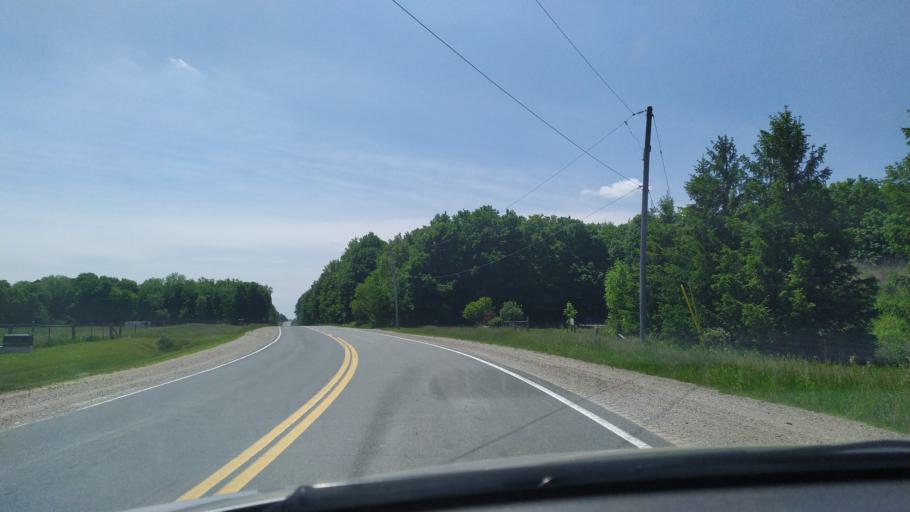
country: CA
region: Ontario
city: Ingersoll
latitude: 43.0478
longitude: -80.9819
